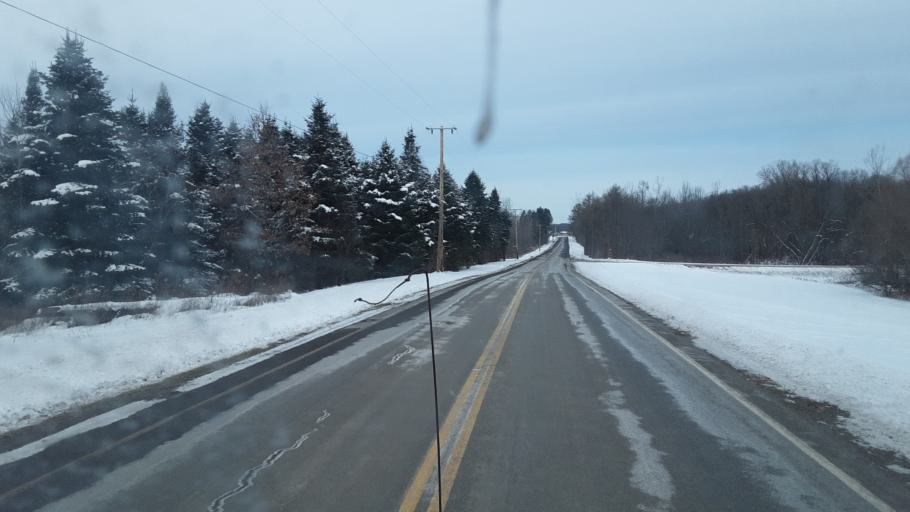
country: US
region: New York
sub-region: Wayne County
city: Lyons
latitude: 43.0987
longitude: -77.0434
